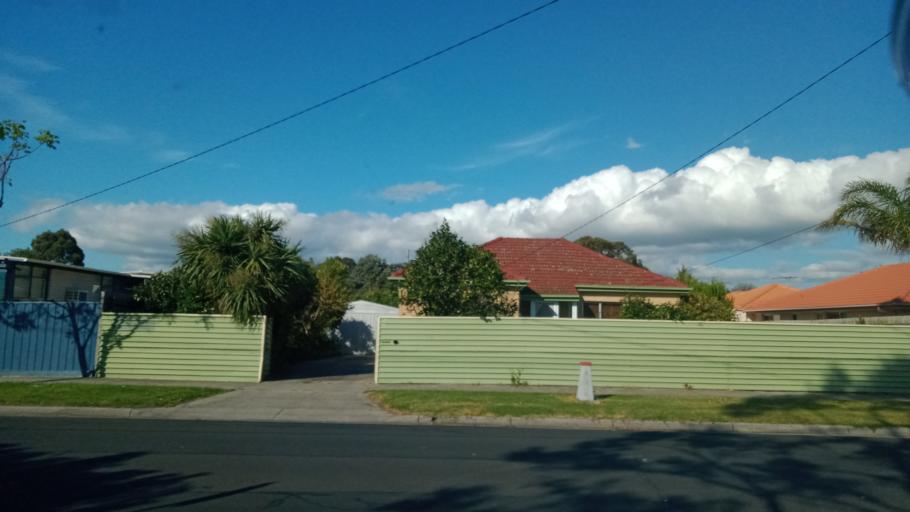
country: AU
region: Victoria
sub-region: Kingston
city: Chelsea
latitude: -38.0473
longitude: 145.1236
